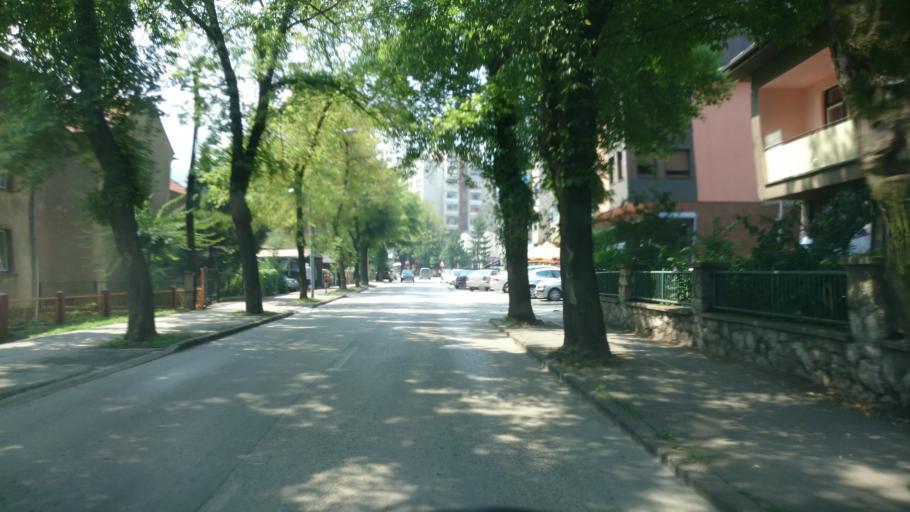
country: BA
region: Federation of Bosnia and Herzegovina
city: Zenica
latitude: 44.1996
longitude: 17.8992
